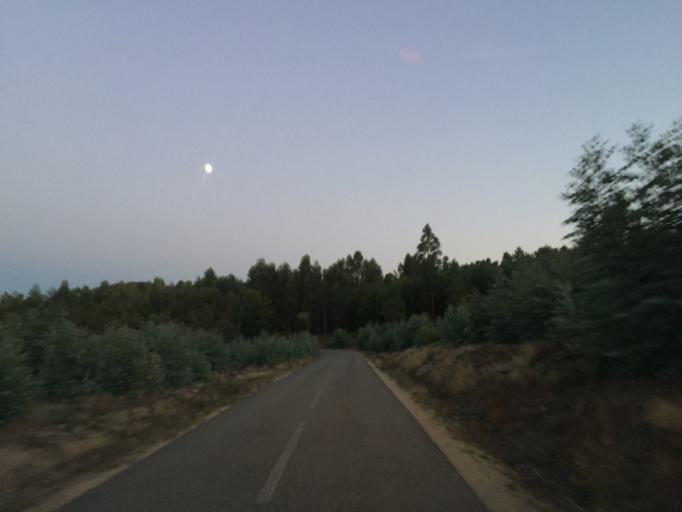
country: PT
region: Portalegre
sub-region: Castelo de Vide
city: Castelo de Vide
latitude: 39.4050
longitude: -7.4583
